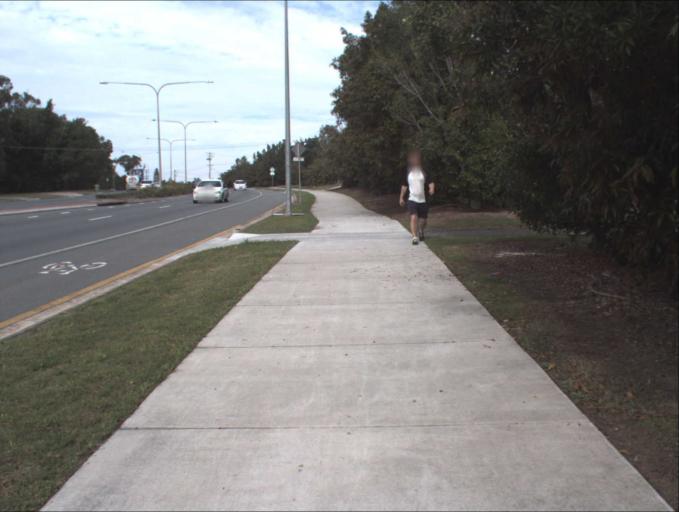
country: AU
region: Queensland
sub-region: Logan
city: Woodridge
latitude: -27.6569
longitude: 153.0648
